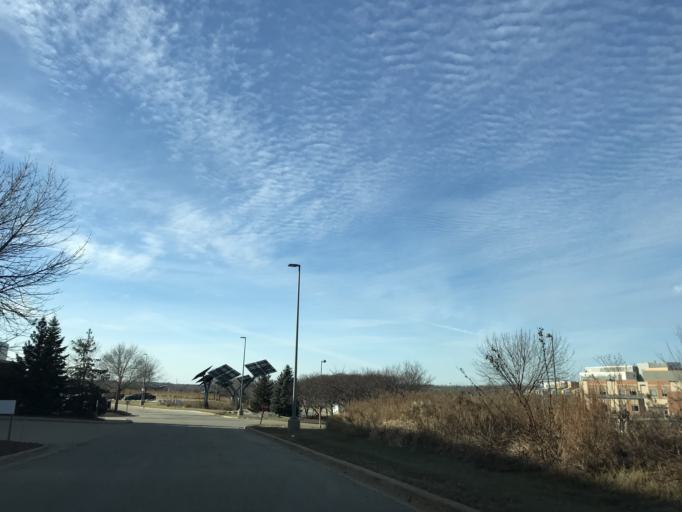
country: US
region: Wisconsin
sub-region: Dane County
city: Windsor
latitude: 43.1520
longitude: -89.2956
